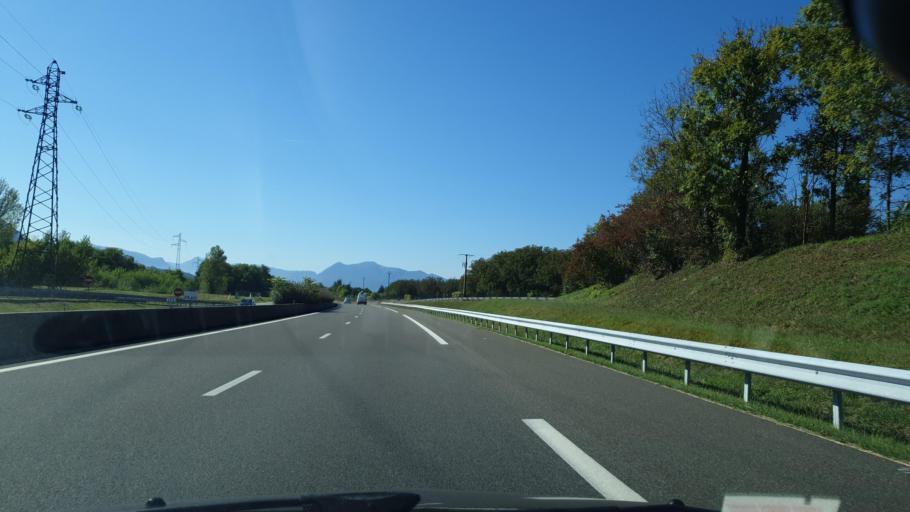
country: FR
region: Rhone-Alpes
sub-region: Departement de l'Isere
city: Saint-Sauveur
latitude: 45.1584
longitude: 5.3608
